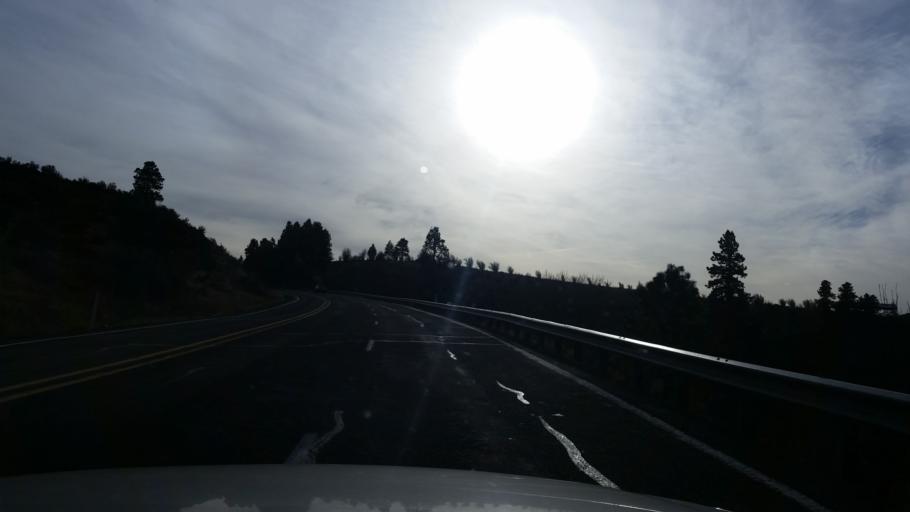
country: US
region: Washington
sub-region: Kittitas County
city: Ellensburg
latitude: 47.1209
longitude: -120.7242
